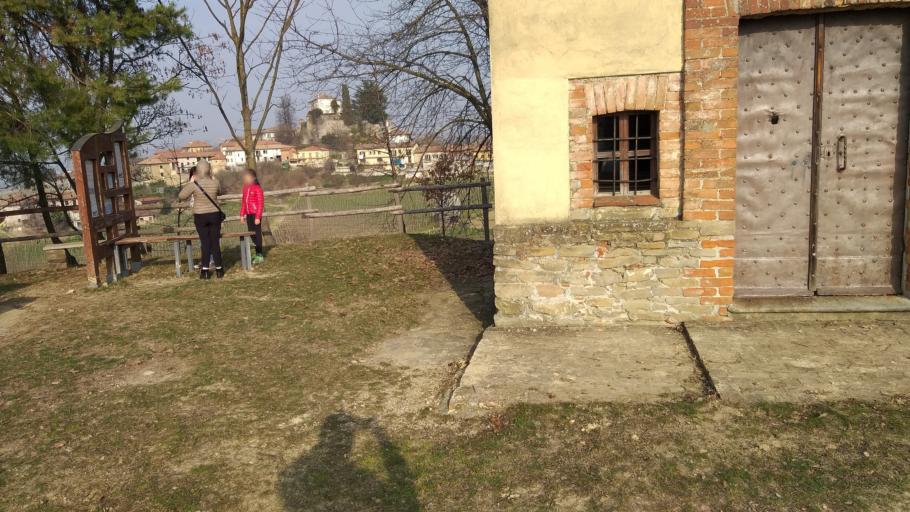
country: IT
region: Piedmont
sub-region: Provincia di Cuneo
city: Castiglione Falletto
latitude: 44.6087
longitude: 7.9710
